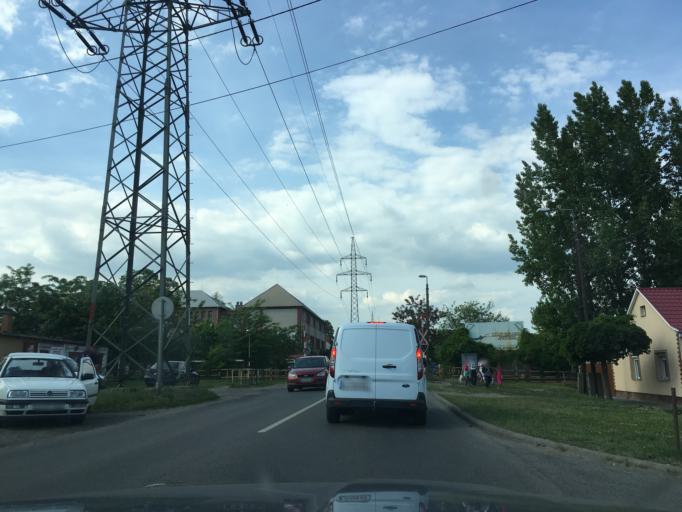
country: HU
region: Hajdu-Bihar
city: Debrecen
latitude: 47.5272
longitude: 21.6601
